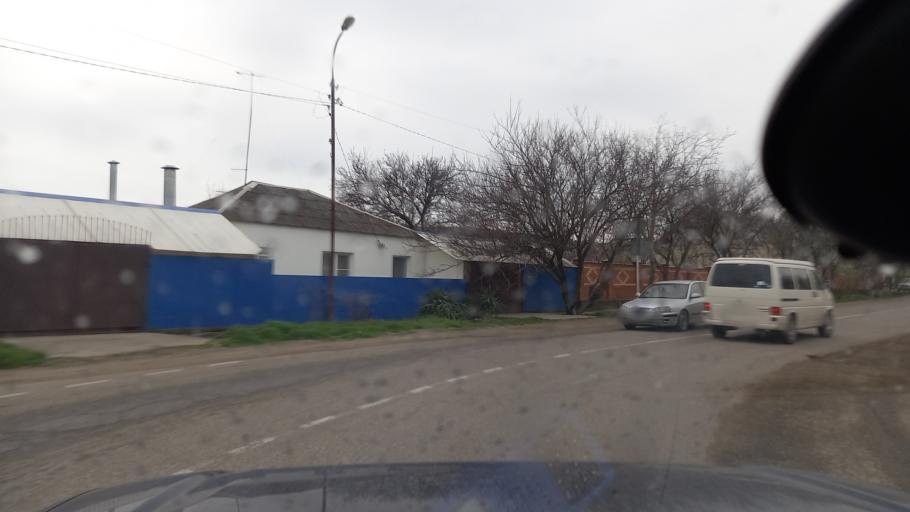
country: RU
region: Krasnodarskiy
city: Sukko
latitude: 44.8599
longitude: 37.4394
